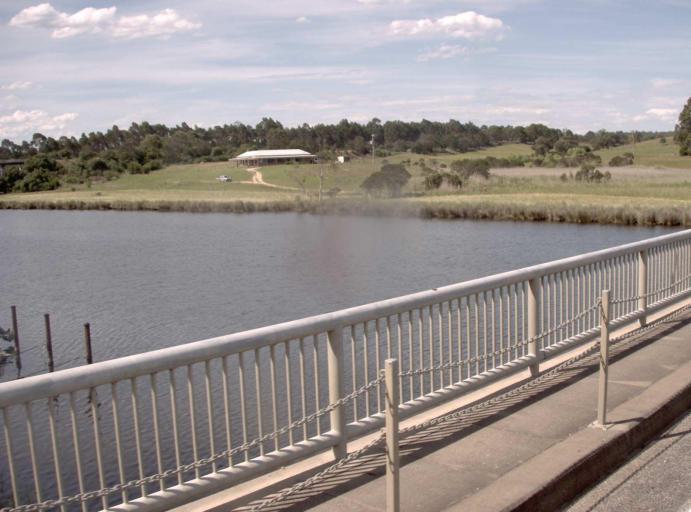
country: AU
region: Victoria
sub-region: East Gippsland
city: Bairnsdale
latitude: -37.8160
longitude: 147.7400
